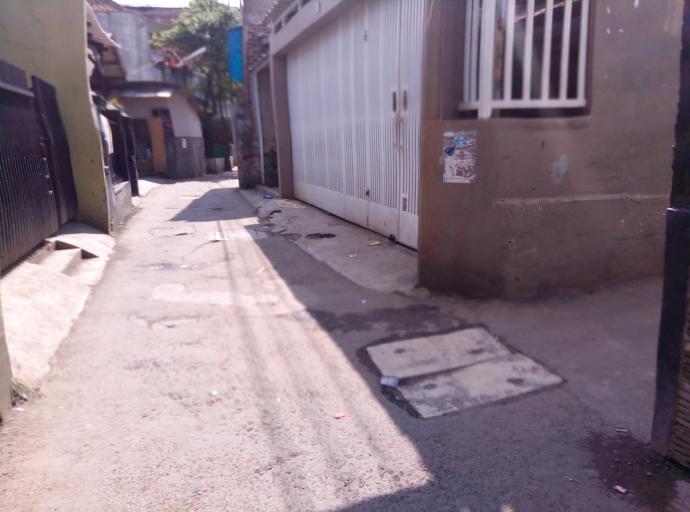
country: ID
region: West Java
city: Bandung
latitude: -6.9266
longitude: 107.6474
